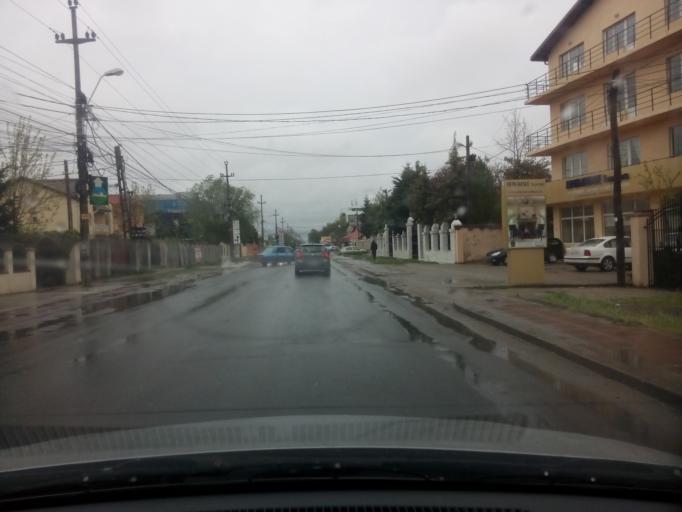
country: RO
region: Ilfov
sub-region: Voluntari City
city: Voluntari
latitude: 44.5094
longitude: 26.1384
